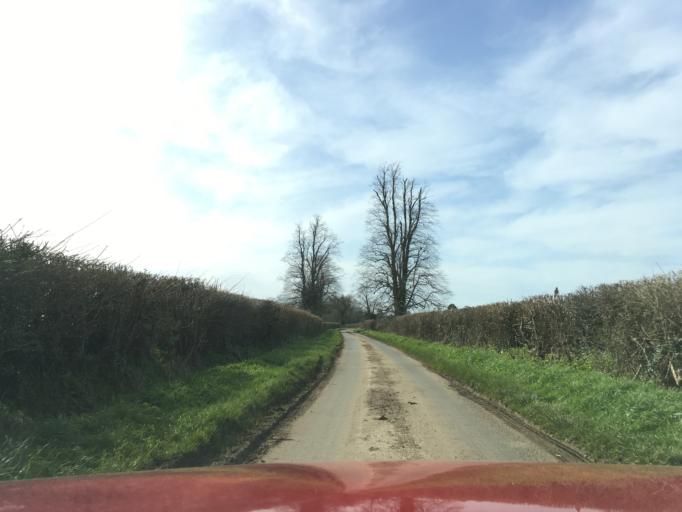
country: GB
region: England
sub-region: Wiltshire
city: Luckington
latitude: 51.5428
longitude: -2.2233
